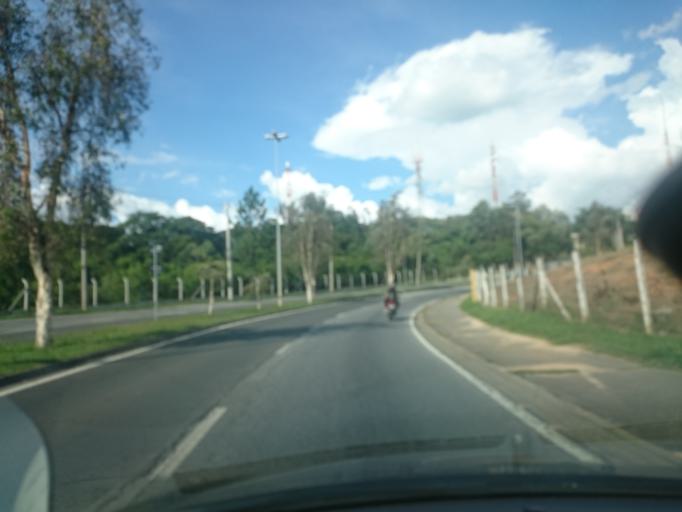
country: BR
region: Sao Paulo
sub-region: Sorocaba
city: Sorocaba
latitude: -23.4825
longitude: -47.4255
